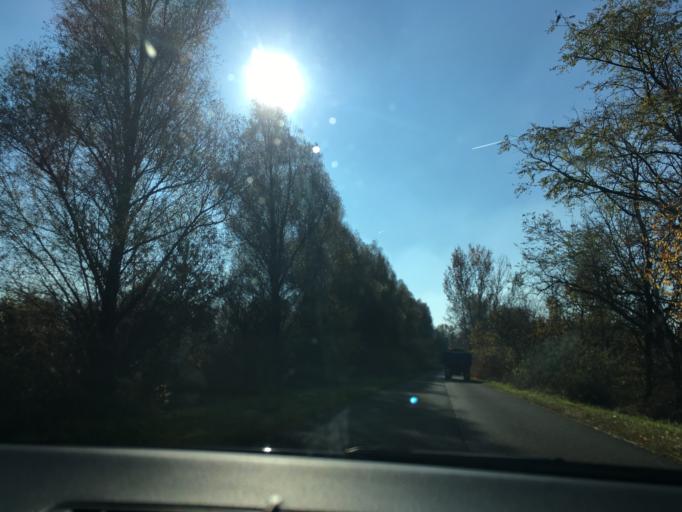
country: HU
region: Hajdu-Bihar
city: Hajdusamson
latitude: 47.5074
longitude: 21.7388
